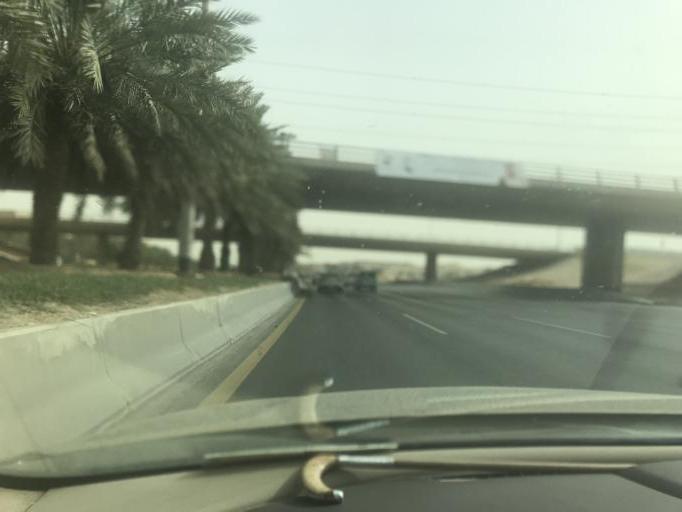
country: SA
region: Ar Riyad
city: Riyadh
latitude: 24.8103
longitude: 46.7137
